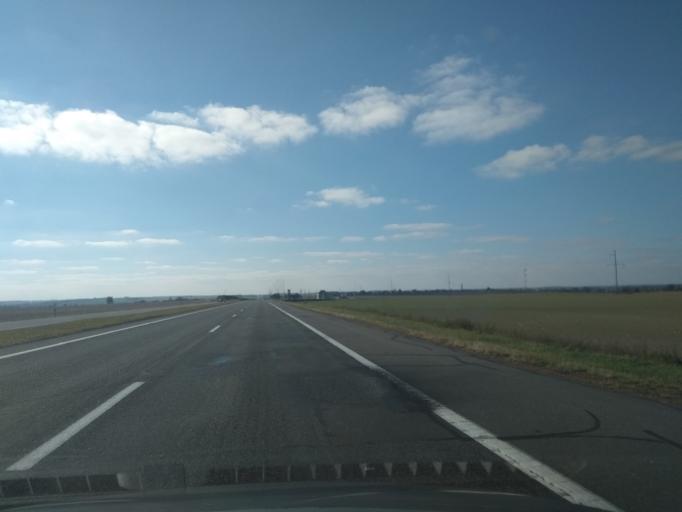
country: BY
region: Minsk
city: Haradzyeya
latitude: 53.3590
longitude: 26.4725
